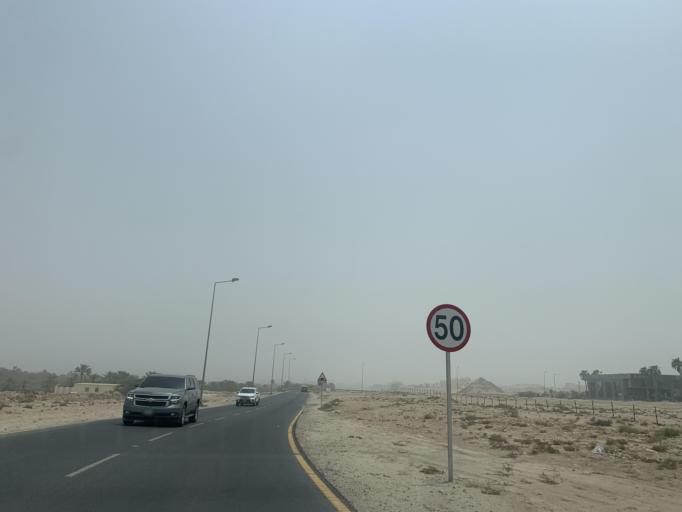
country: BH
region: Central Governorate
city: Madinat Hamad
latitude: 26.1734
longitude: 50.4841
